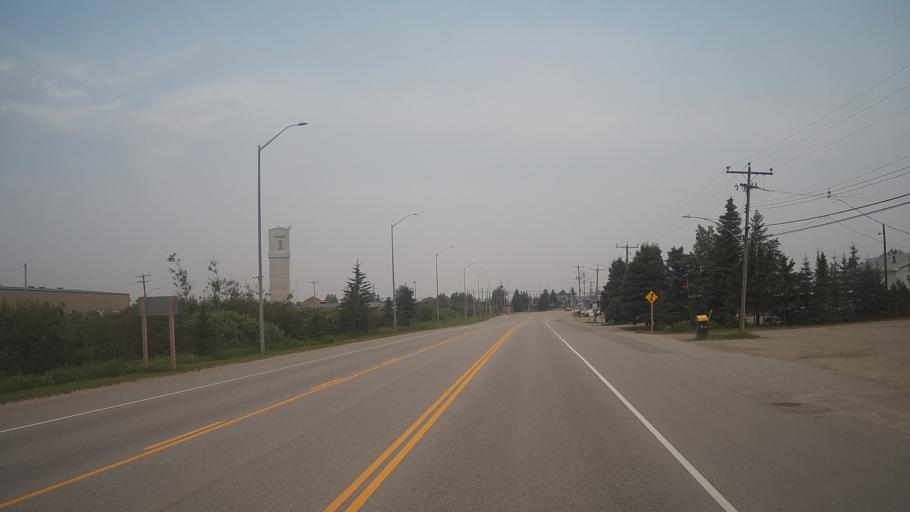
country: CA
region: Ontario
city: Hearst
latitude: 49.6877
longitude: -83.6452
